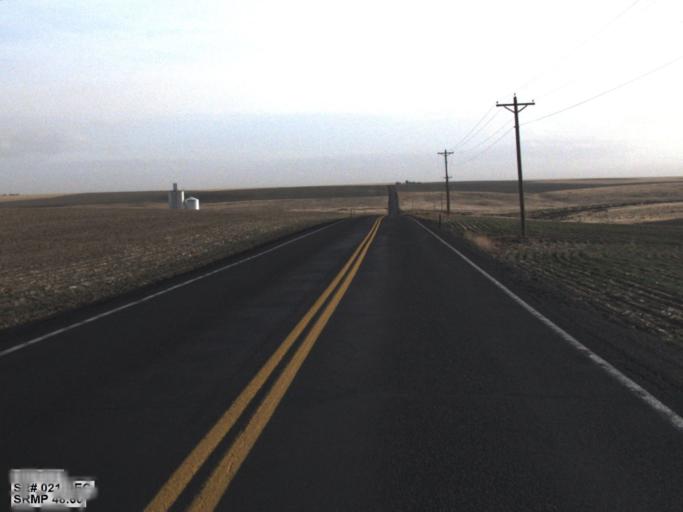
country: US
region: Washington
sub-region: Adams County
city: Ritzville
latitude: 47.2361
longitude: -118.6862
